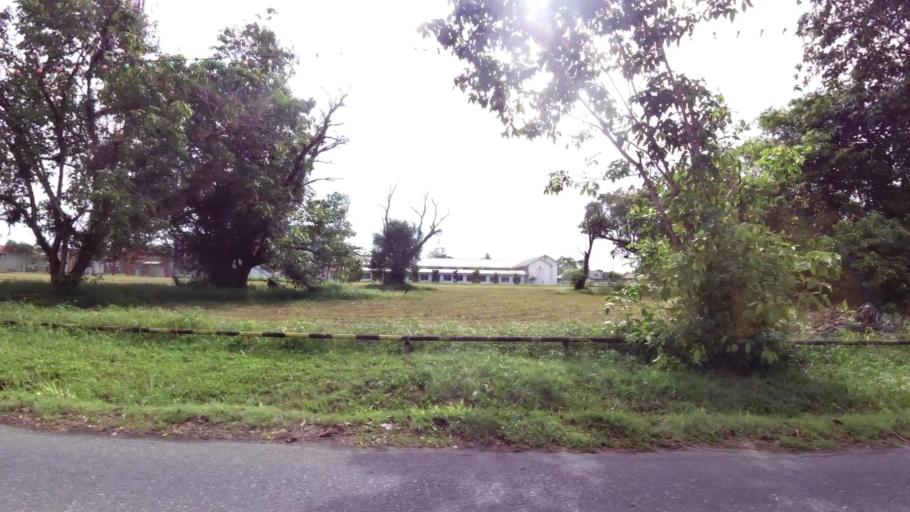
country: BN
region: Belait
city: Seria
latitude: 4.6130
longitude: 114.3317
